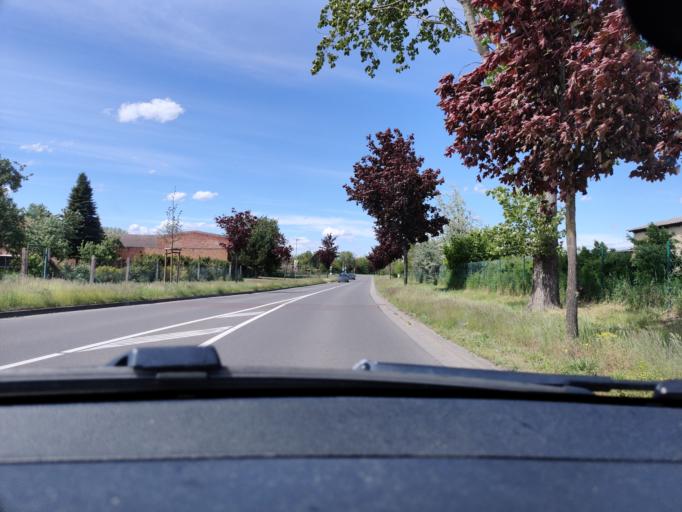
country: DE
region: Saxony-Anhalt
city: Mockern
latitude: 52.1904
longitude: 11.9080
